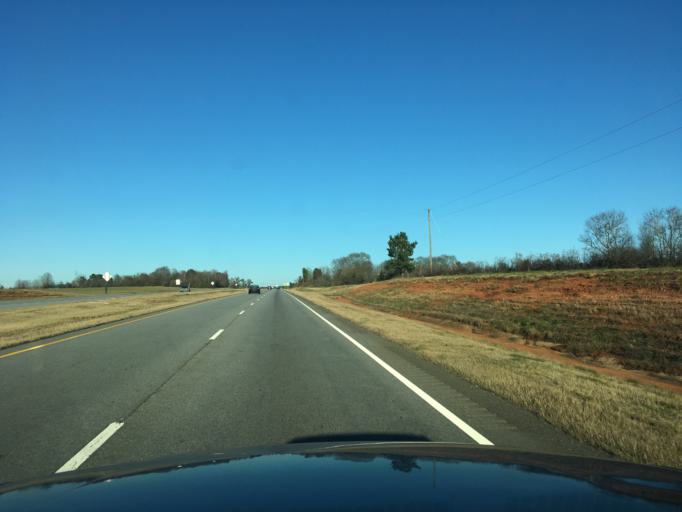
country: US
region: Georgia
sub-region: Carroll County
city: Carrollton
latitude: 33.4807
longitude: -85.1021
